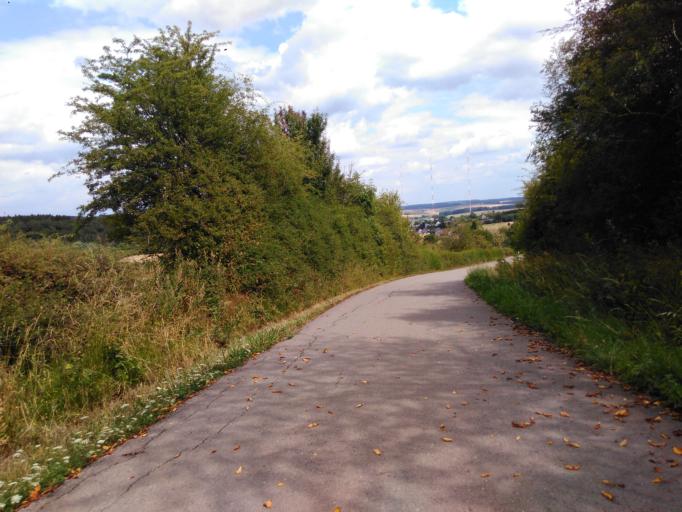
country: LU
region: Grevenmacher
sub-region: Canton de Grevenmacher
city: Junglinster
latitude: 49.7250
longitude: 6.2836
